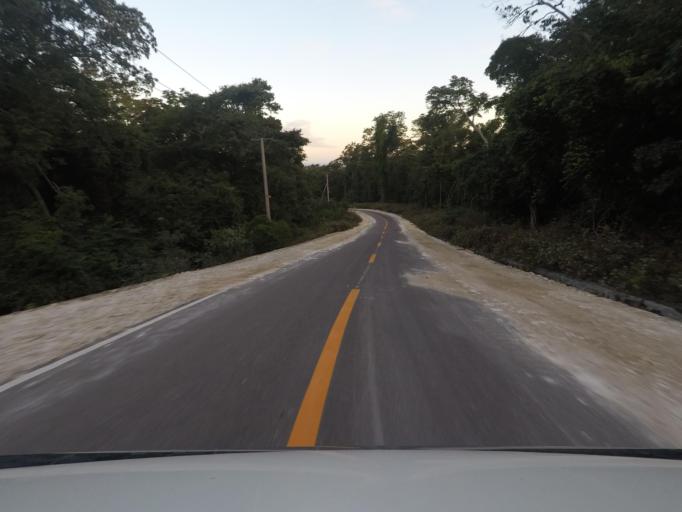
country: TL
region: Lautem
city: Lospalos
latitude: -8.4017
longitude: 127.2848
